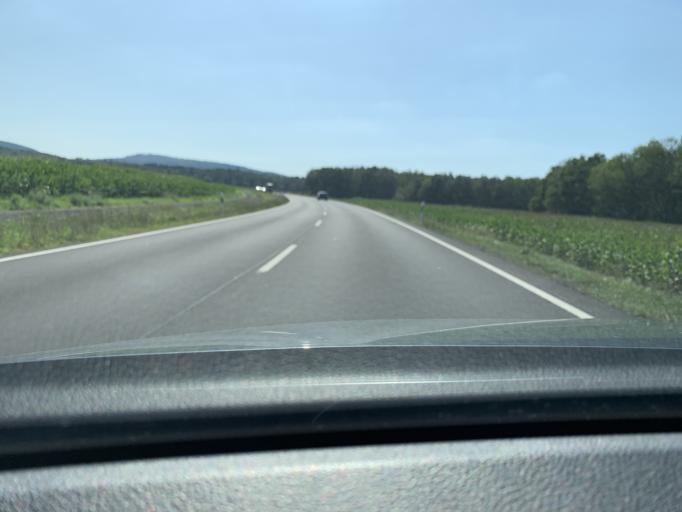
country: DE
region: Bavaria
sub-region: Upper Franconia
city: Ebersdorf
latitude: 50.3180
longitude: 11.1458
